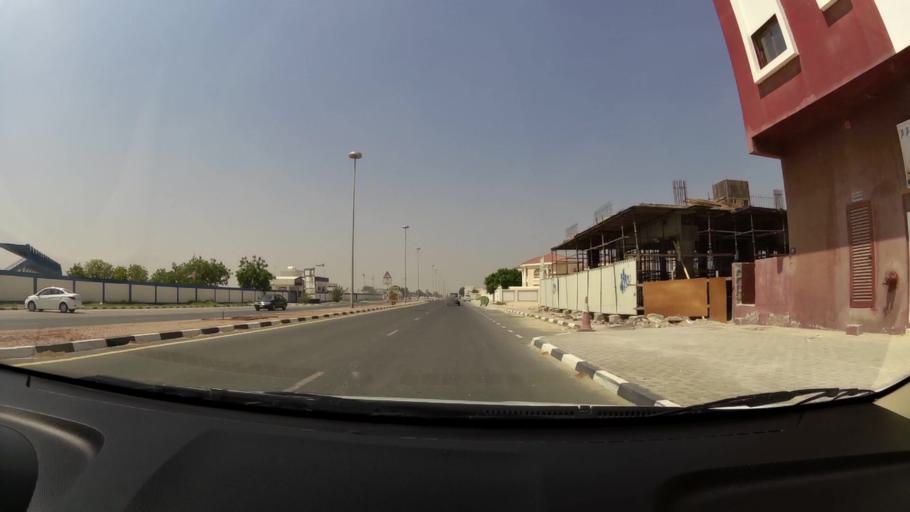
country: AE
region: Umm al Qaywayn
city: Umm al Qaywayn
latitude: 25.5675
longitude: 55.5582
